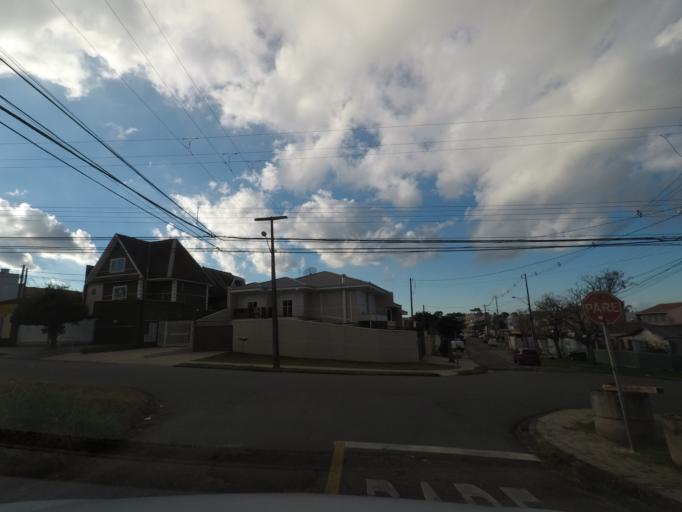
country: BR
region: Parana
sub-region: Sao Jose Dos Pinhais
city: Sao Jose dos Pinhais
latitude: -25.5014
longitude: -49.2609
